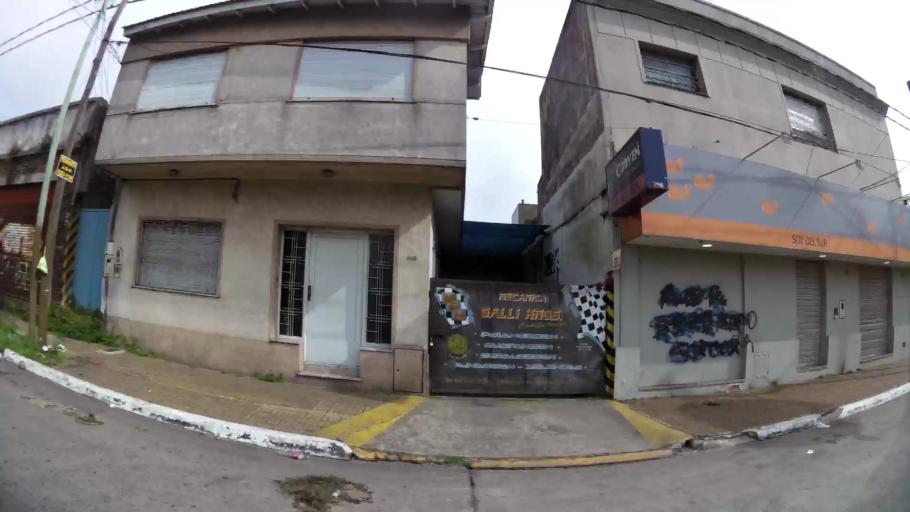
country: AR
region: Buenos Aires
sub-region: Partido de Quilmes
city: Quilmes
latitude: -34.7225
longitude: -58.2456
